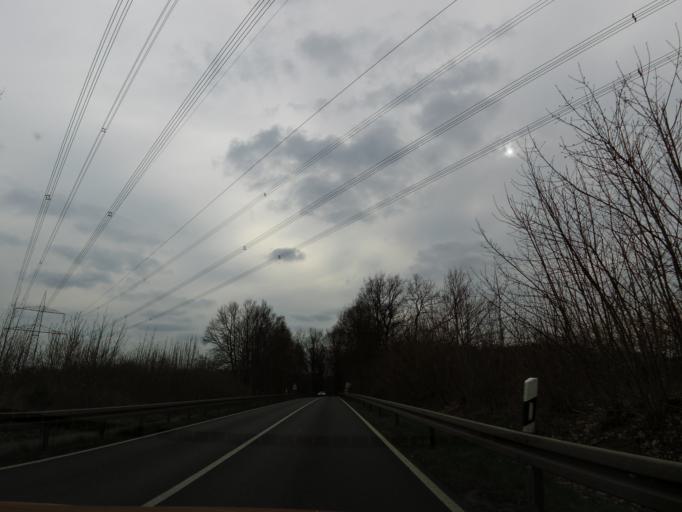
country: DE
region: Brandenburg
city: Mullrose
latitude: 52.2764
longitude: 14.4433
